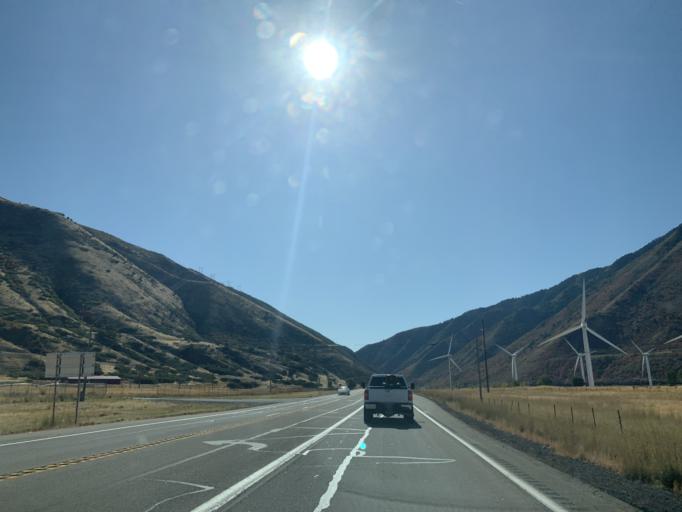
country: US
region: Utah
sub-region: Utah County
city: Mapleton
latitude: 40.0814
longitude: -111.5870
